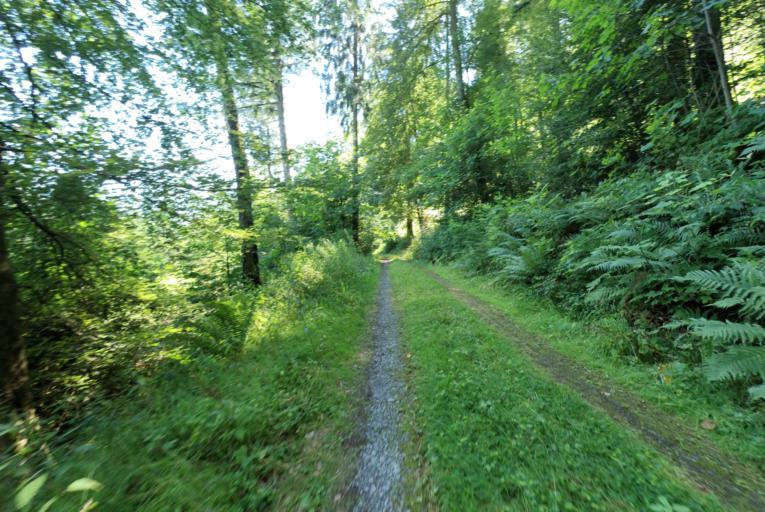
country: DE
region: Baden-Wuerttemberg
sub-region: Karlsruhe Region
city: Zwingenberg
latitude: 49.4009
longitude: 9.0452
